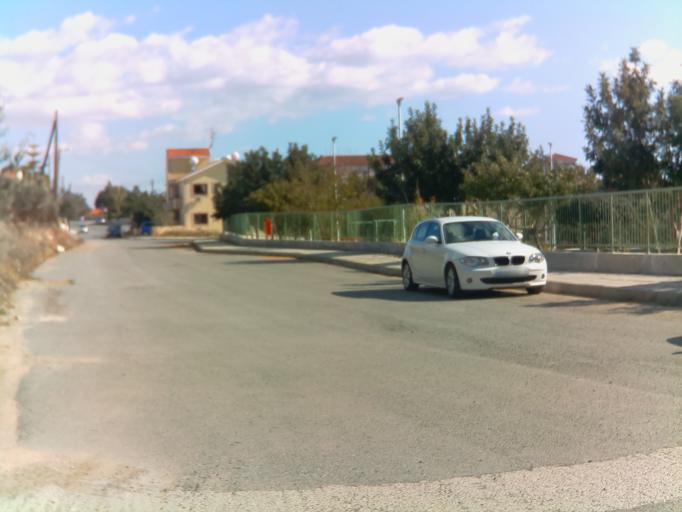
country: CY
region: Limassol
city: Pissouri
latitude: 34.6687
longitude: 32.6960
